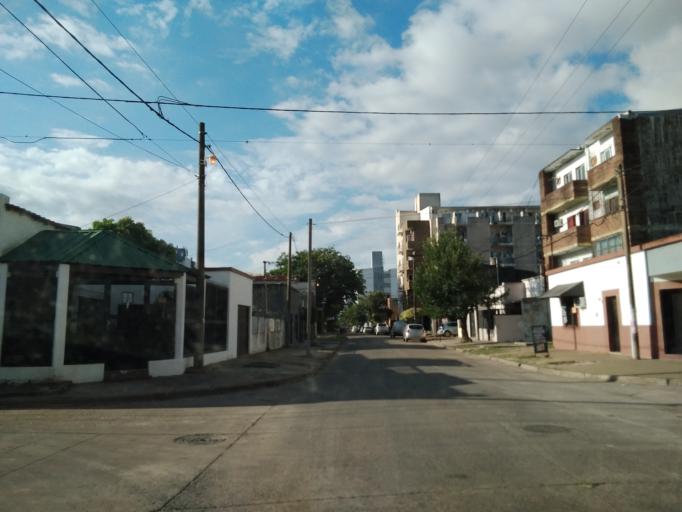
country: AR
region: Corrientes
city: Corrientes
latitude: -27.4638
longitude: -58.8218
